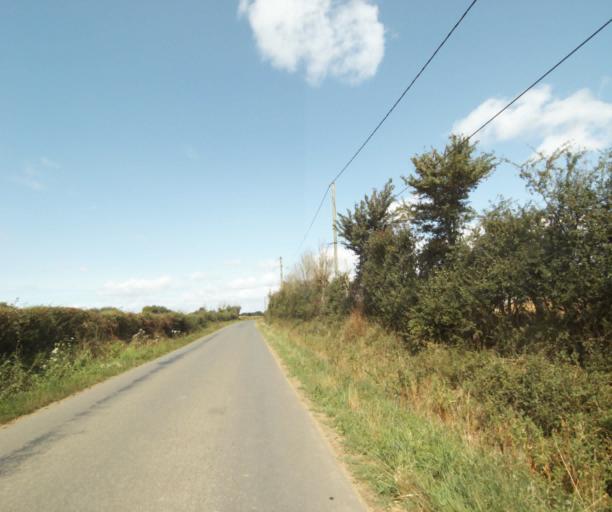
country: FR
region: Pays de la Loire
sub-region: Departement de la Sarthe
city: Sable-sur-Sarthe
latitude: 47.8421
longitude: -0.3693
